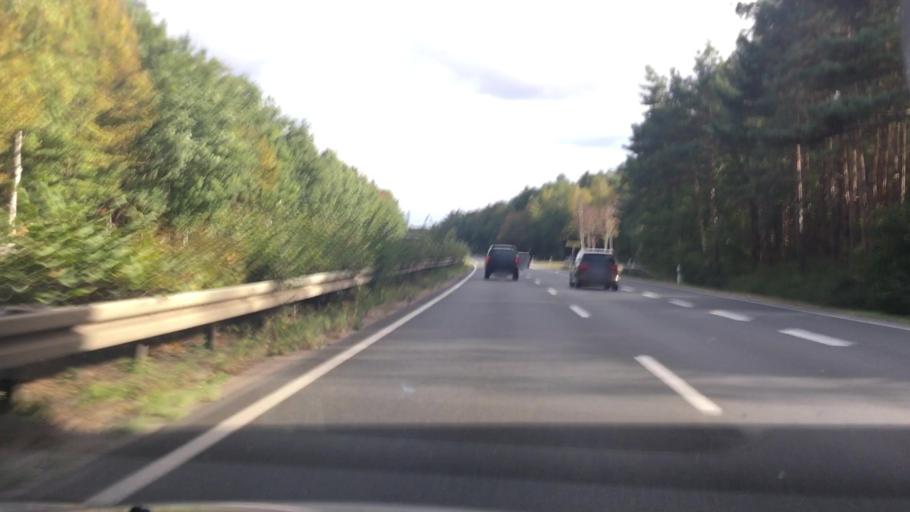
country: DE
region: Lower Saxony
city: Neustadt am Rubenberge
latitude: 52.4889
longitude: 9.4886
